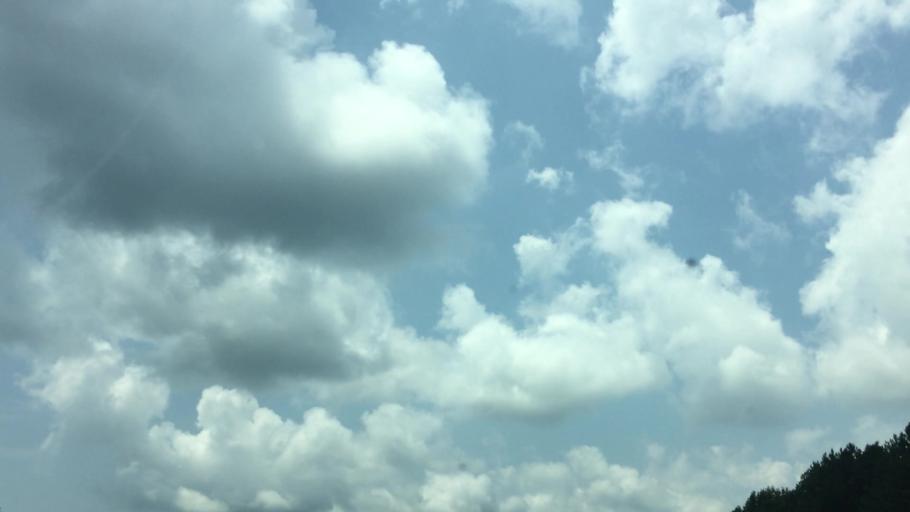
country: US
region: Georgia
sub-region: Fulton County
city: Palmetto
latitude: 33.5729
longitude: -84.6821
